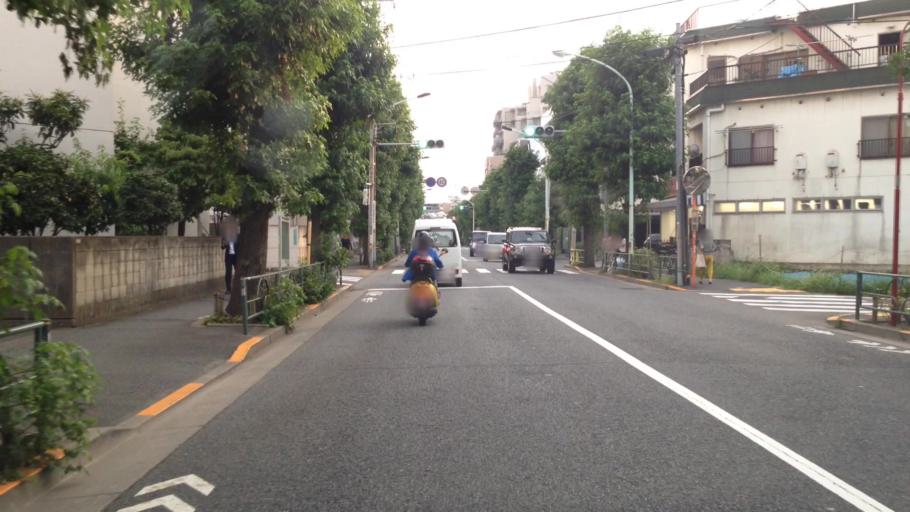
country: JP
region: Tokyo
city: Tokyo
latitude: 35.6313
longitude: 139.6851
